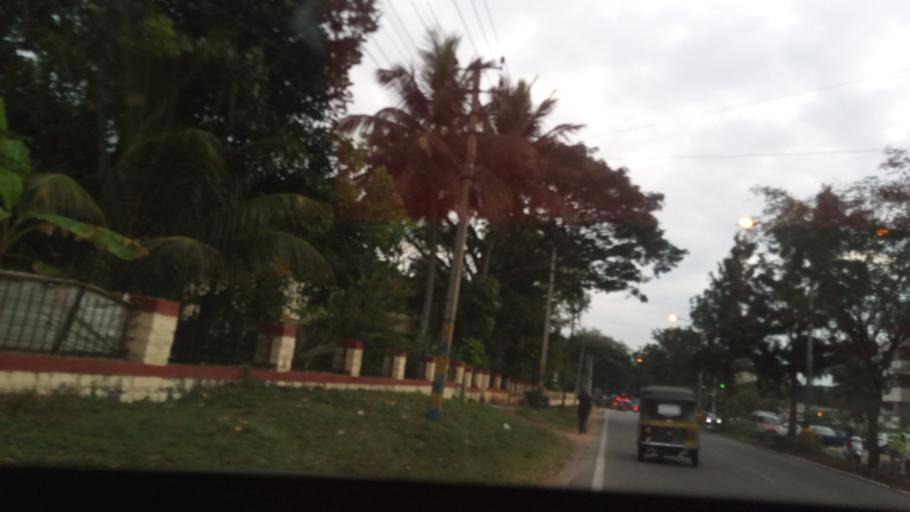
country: IN
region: Karnataka
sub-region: Mysore
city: Mysore
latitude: 12.3286
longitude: 76.6332
